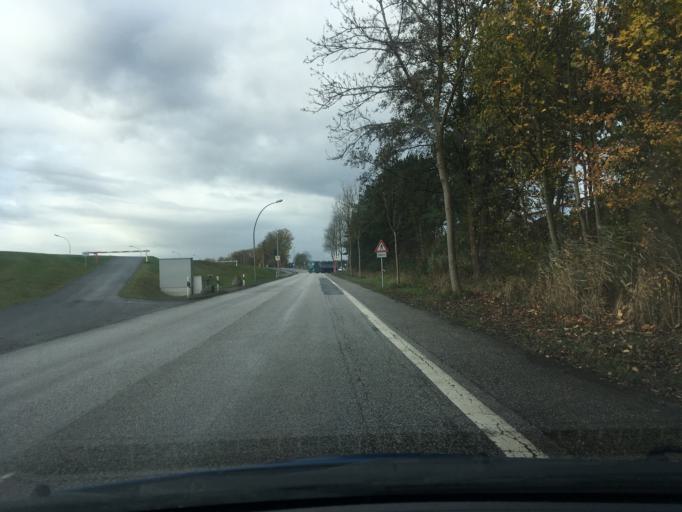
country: DE
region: Schleswig-Holstein
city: Escheburg
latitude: 53.4356
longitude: 10.3241
